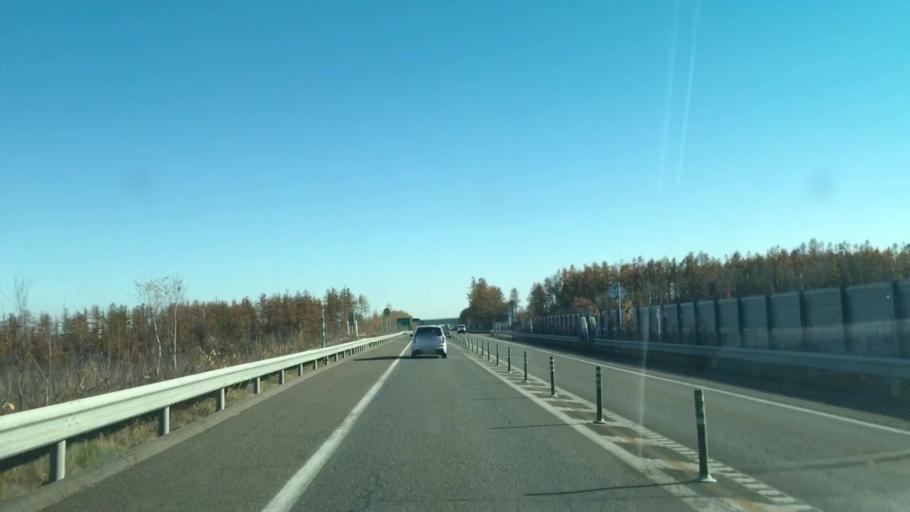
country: JP
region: Hokkaido
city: Otofuke
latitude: 43.0021
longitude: 142.8479
